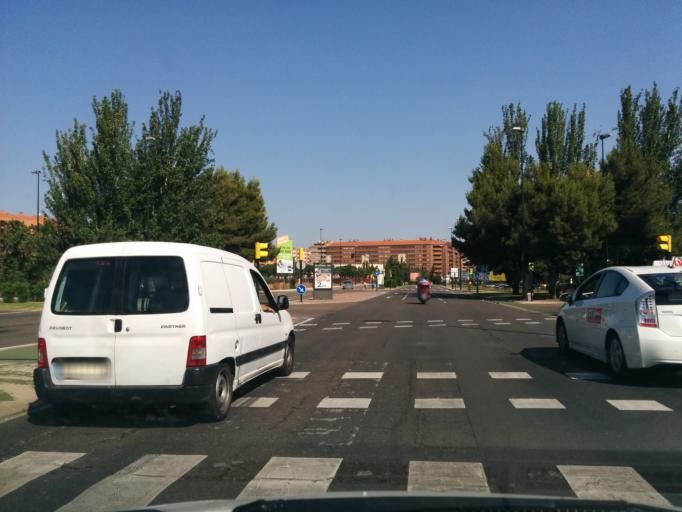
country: ES
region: Aragon
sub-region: Provincia de Zaragoza
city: Zaragoza
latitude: 41.6580
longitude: -0.8611
